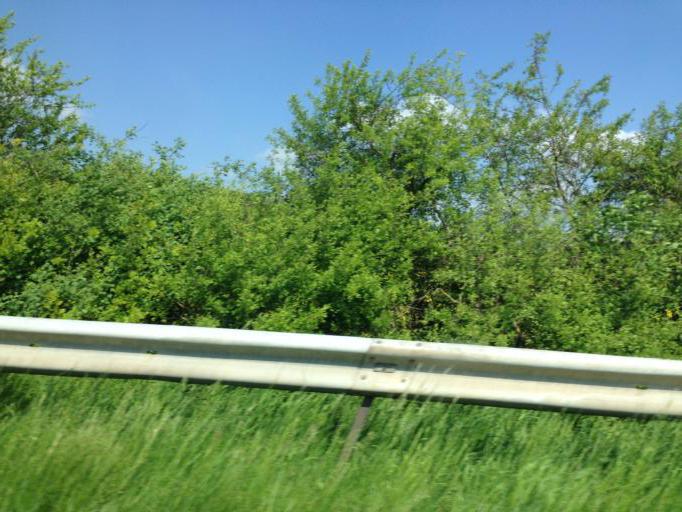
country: DE
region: North Rhine-Westphalia
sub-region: Regierungsbezirk Koln
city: Mechernich
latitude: 50.5683
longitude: 6.6995
